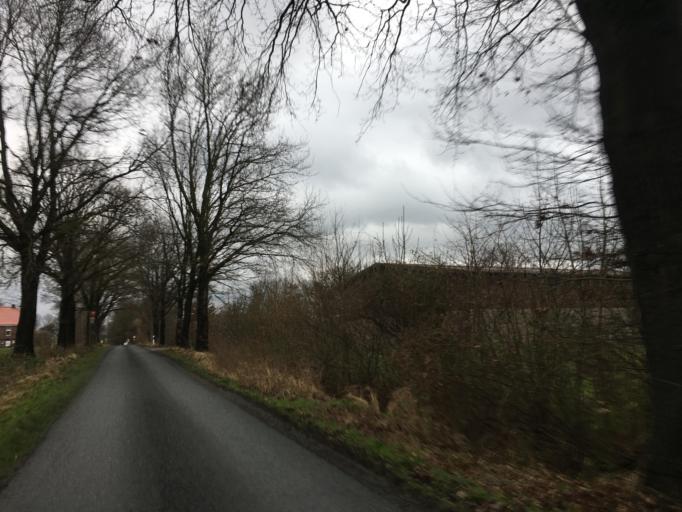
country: DE
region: North Rhine-Westphalia
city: Olfen
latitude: 51.7536
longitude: 7.3501
